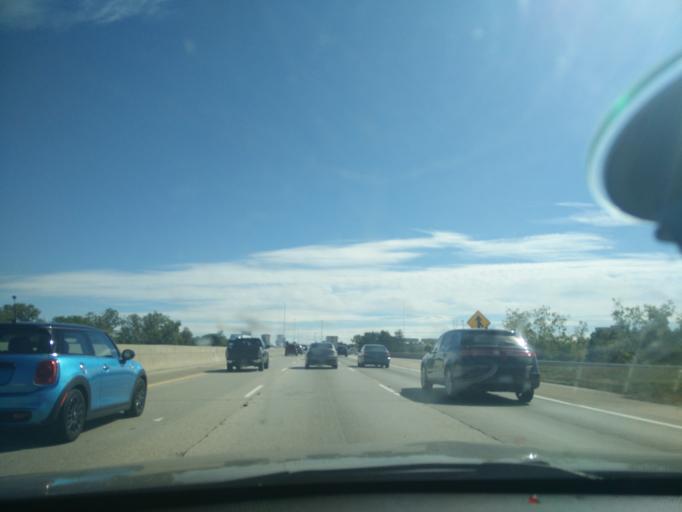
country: US
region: Michigan
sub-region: Oakland County
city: Bingham Farms
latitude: 42.4879
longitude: -83.2800
